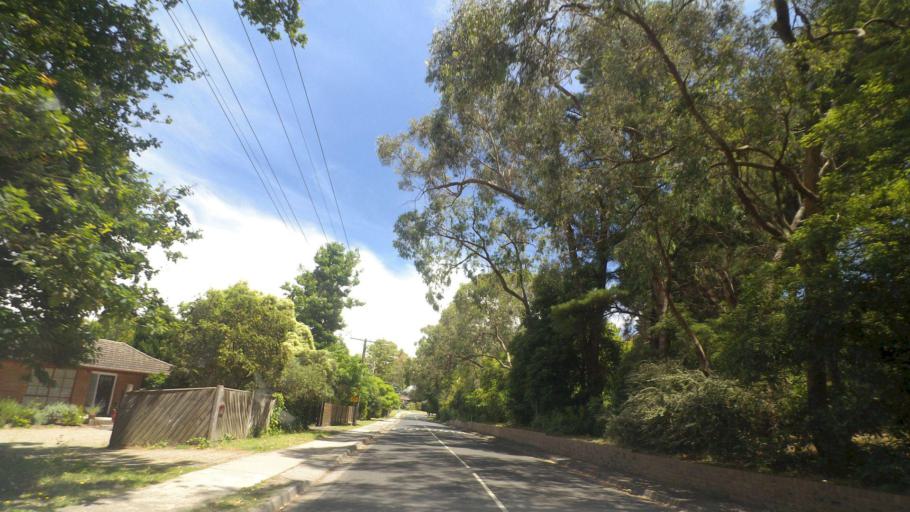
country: AU
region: Victoria
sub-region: Knox
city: Boronia
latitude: -37.8565
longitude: 145.2910
